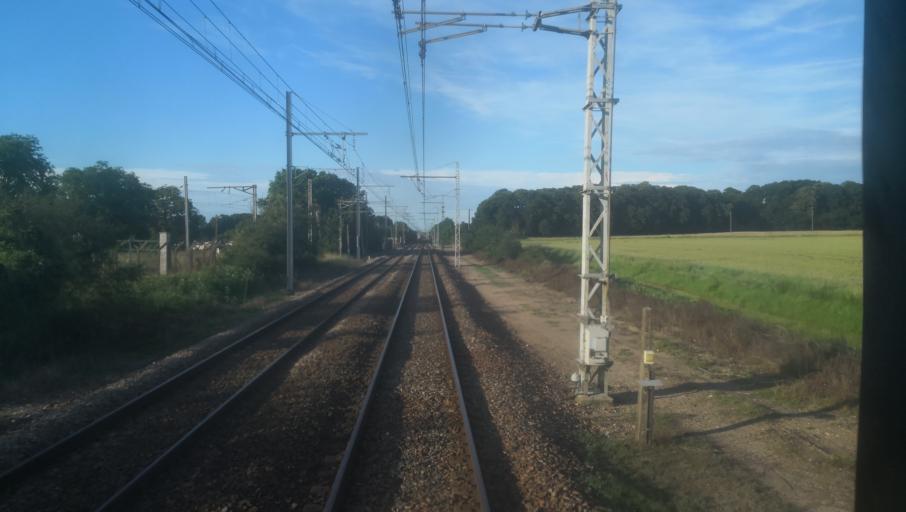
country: FR
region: Centre
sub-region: Departement de l'Indre
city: Neuvy-Pailloux
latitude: 46.8780
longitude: 1.8549
